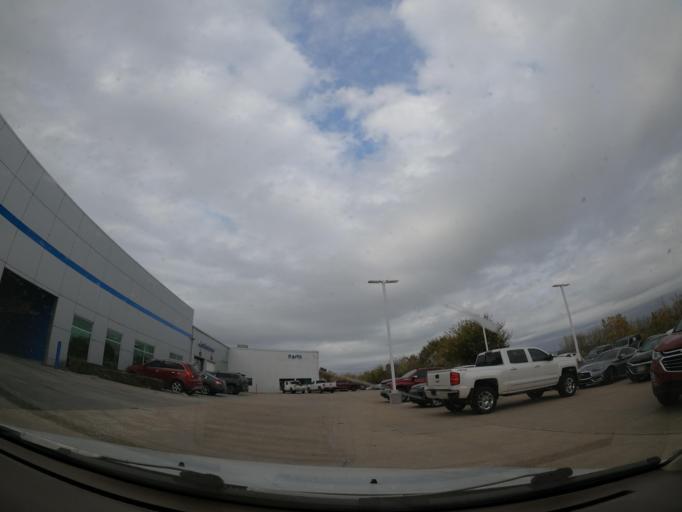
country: US
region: Oklahoma
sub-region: Tulsa County
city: Tulsa
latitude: 36.0910
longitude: -95.9967
